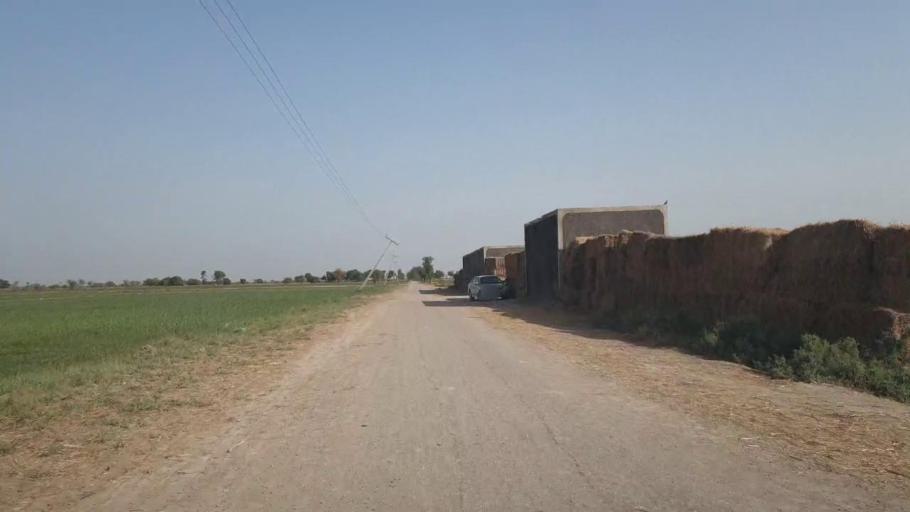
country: PK
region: Sindh
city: Dhoro Naro
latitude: 25.4626
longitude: 69.5584
